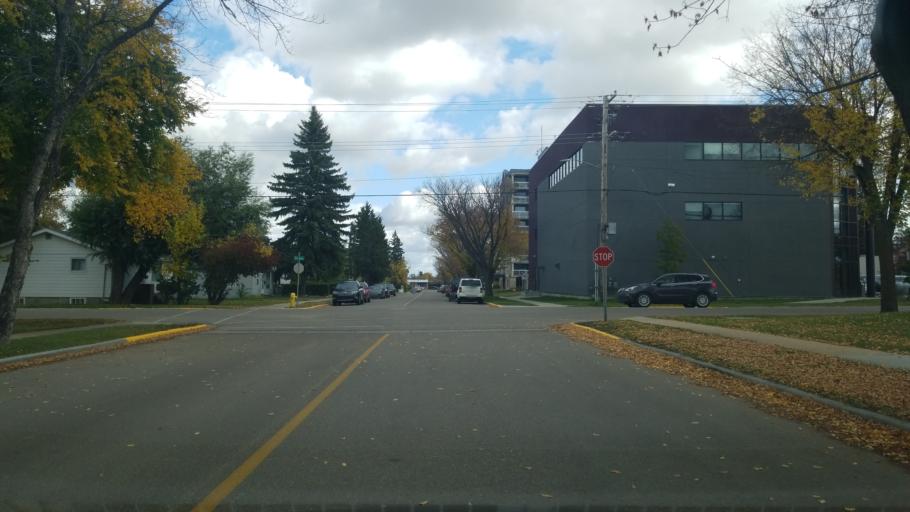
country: CA
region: Saskatchewan
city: Lloydminster
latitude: 53.2807
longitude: -110.0110
